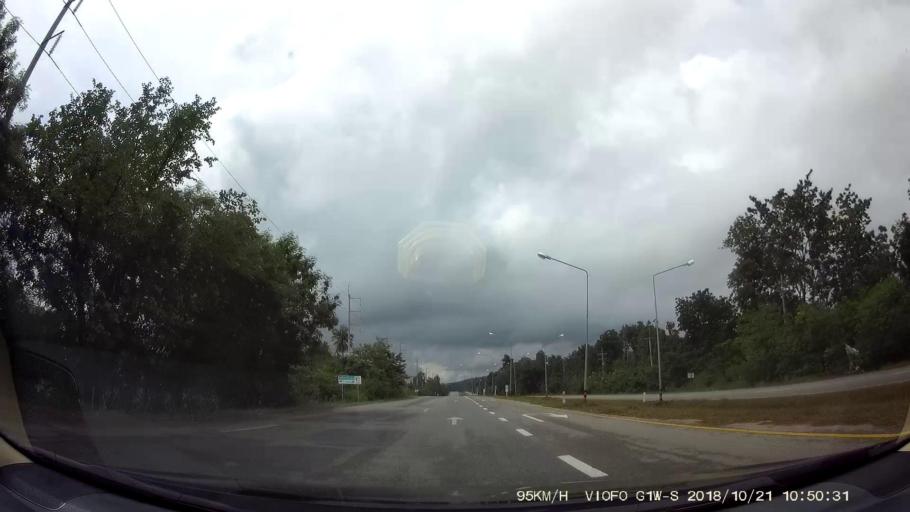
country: TH
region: Chaiyaphum
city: Khon Sawan
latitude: 15.9959
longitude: 102.2158
